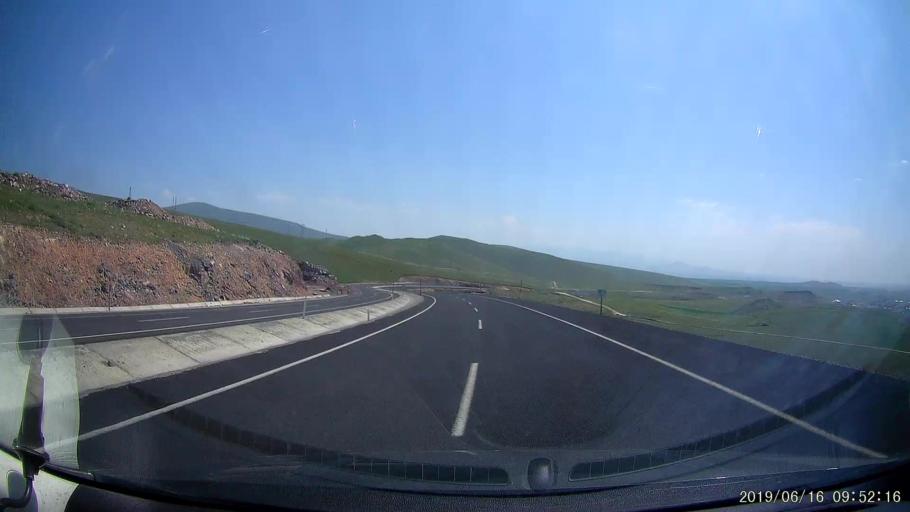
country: TR
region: Kars
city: Digor
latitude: 40.3927
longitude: 43.3836
